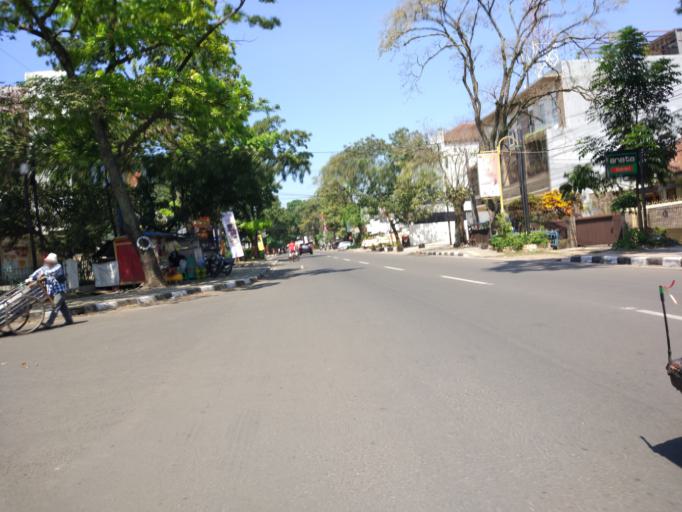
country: ID
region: West Java
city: Bandung
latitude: -6.9254
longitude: 107.6198
